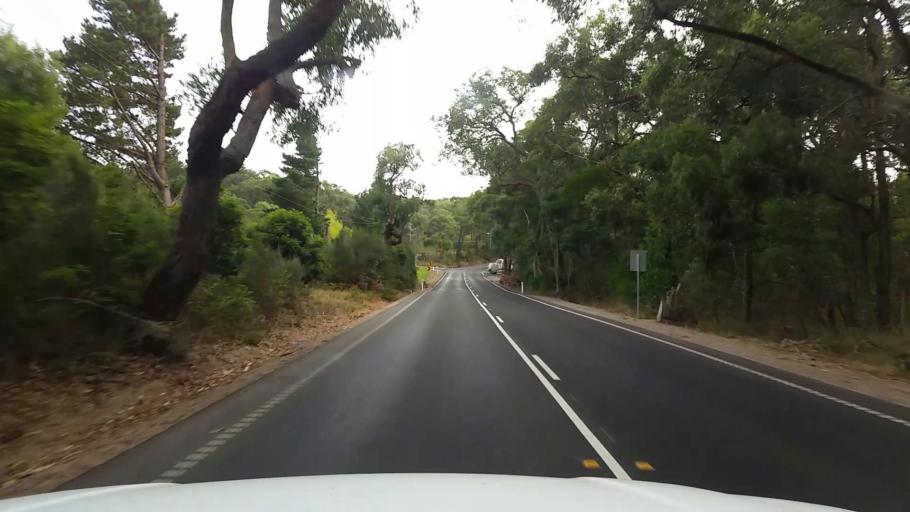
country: AU
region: Victoria
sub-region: Mornington Peninsula
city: Balnarring
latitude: -38.3400
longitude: 145.0979
